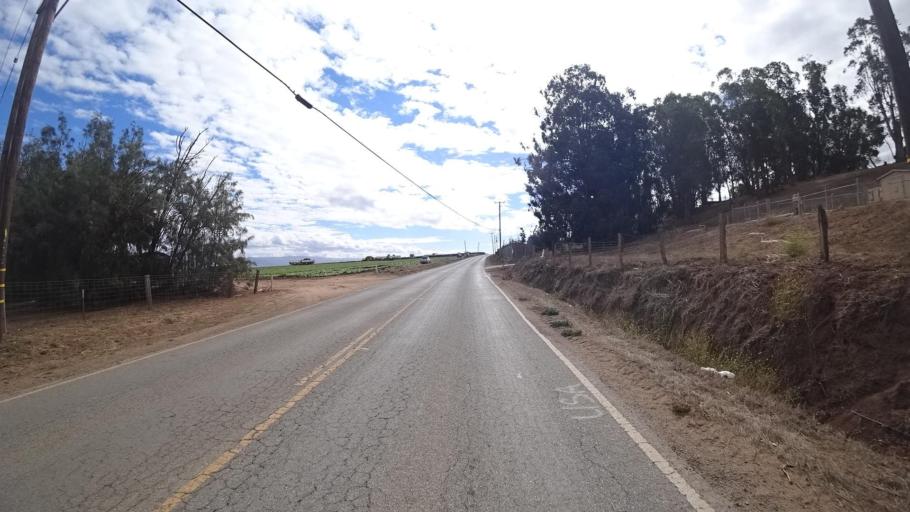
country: US
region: California
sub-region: Monterey County
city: Salinas
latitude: 36.5936
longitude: -121.6114
